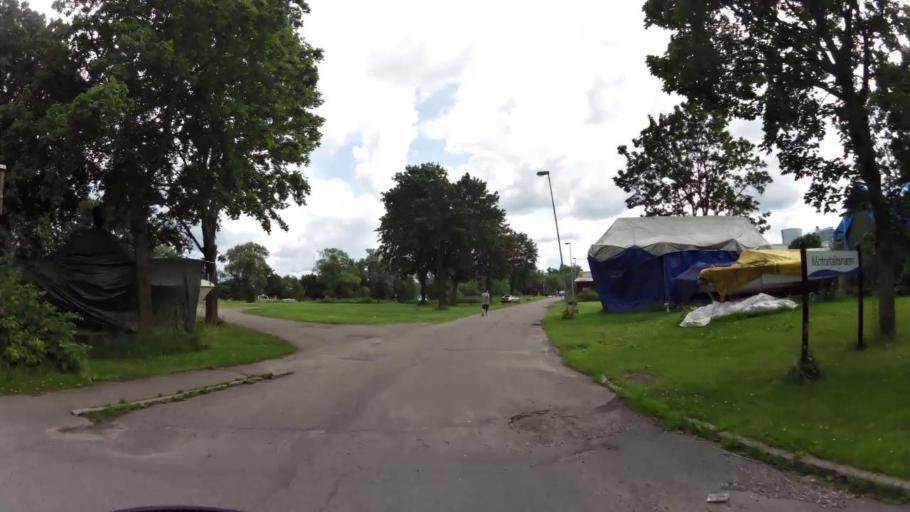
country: SE
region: OEstergoetland
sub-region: Linkopings Kommun
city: Linkoping
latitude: 58.4255
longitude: 15.6286
